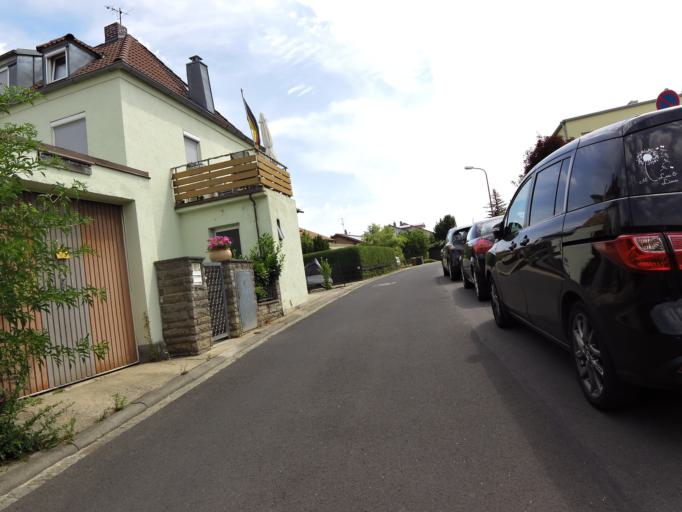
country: DE
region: Bavaria
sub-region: Regierungsbezirk Unterfranken
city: Randersacker
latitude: 49.7604
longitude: 9.9507
